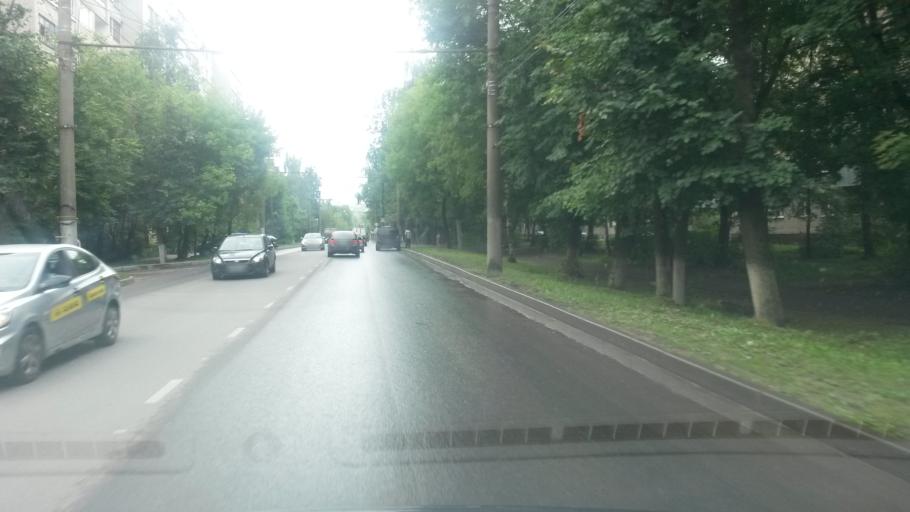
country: RU
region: Ivanovo
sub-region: Gorod Ivanovo
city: Ivanovo
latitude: 57.0055
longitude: 40.9538
